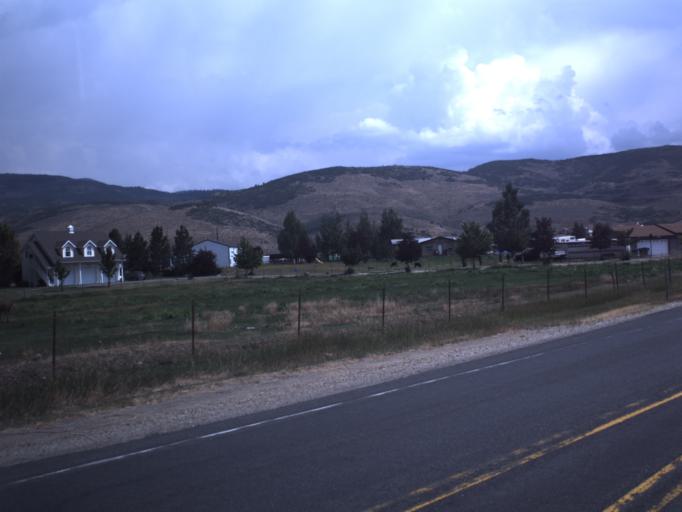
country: US
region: Utah
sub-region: Summit County
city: Francis
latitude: 40.6105
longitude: -111.2747
